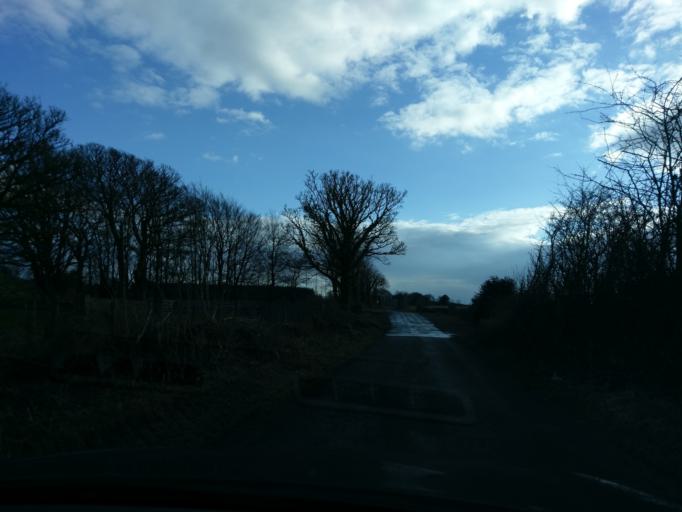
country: IE
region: Connaught
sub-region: County Galway
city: Athenry
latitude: 53.3883
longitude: -8.6238
